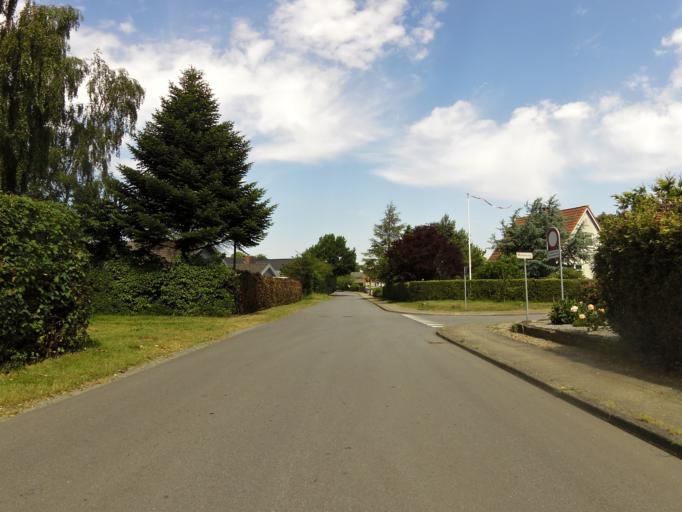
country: DK
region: South Denmark
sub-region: Haderslev Kommune
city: Vojens
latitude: 55.1978
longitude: 9.2104
